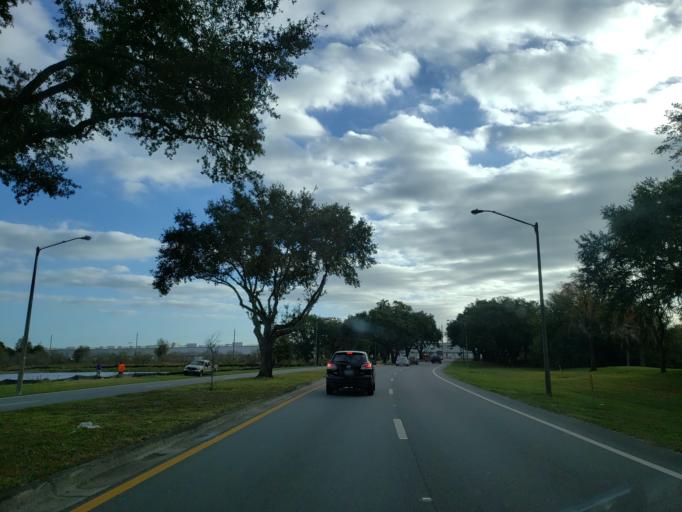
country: US
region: Florida
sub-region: Hillsborough County
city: Plant City
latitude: 27.9897
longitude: -82.1077
